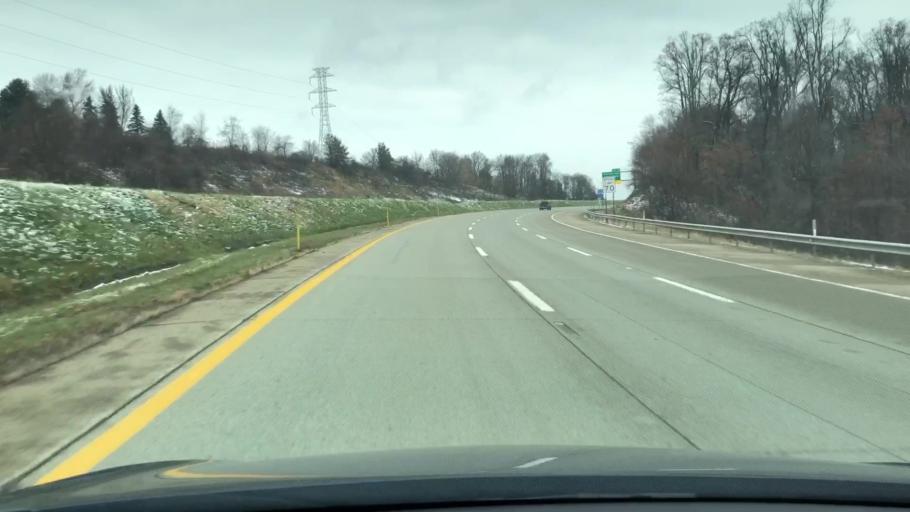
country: US
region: Pennsylvania
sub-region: Westmoreland County
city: Jeannette
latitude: 40.3349
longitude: -79.5809
